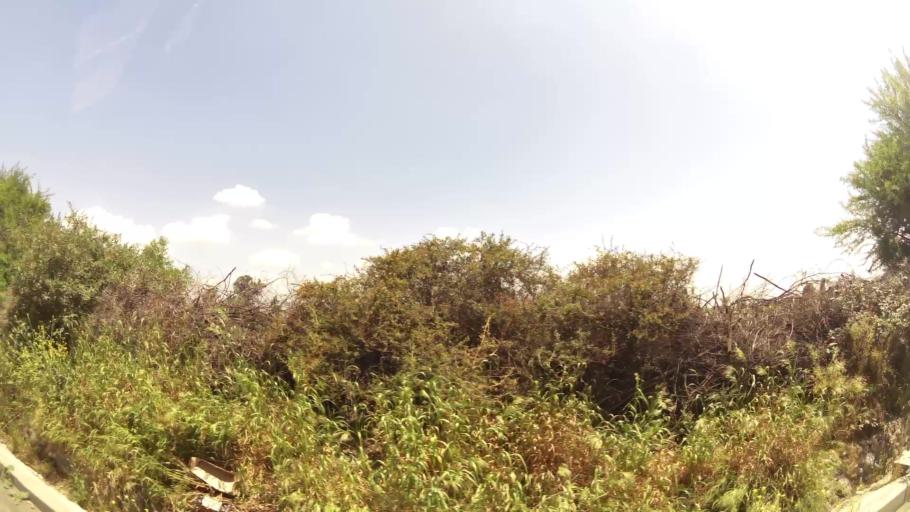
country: CL
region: Santiago Metropolitan
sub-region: Provincia de Maipo
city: San Bernardo
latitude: -33.5731
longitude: -70.7830
